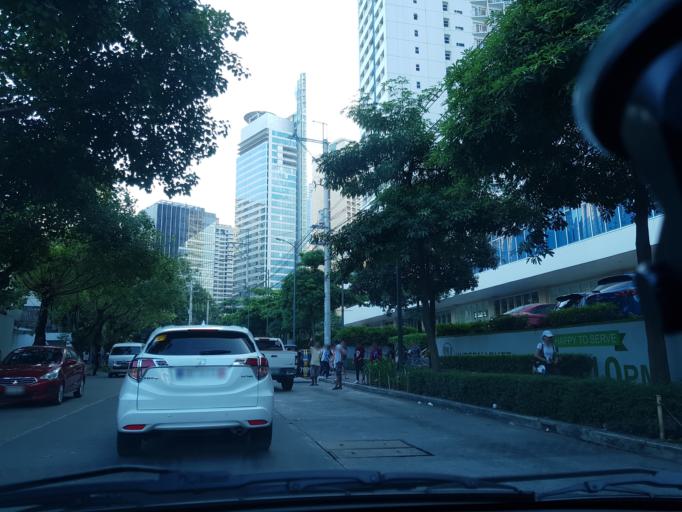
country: PH
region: Metro Manila
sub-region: Makati City
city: Makati City
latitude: 14.5639
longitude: 121.0225
